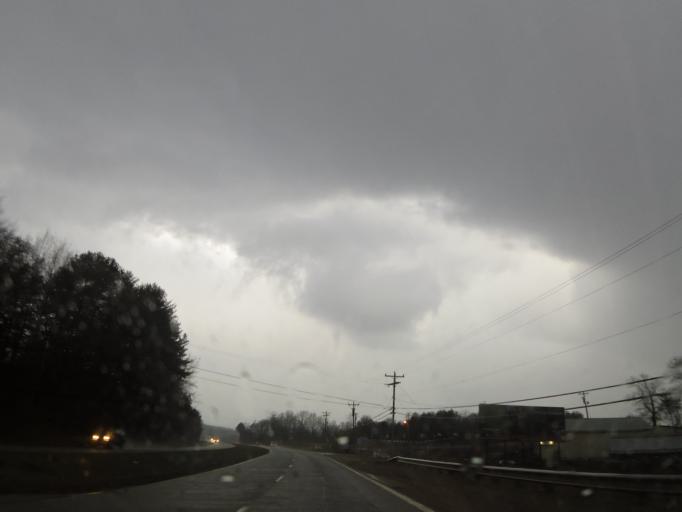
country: US
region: South Carolina
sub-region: Greenville County
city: Travelers Rest
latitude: 35.0200
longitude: -82.4129
